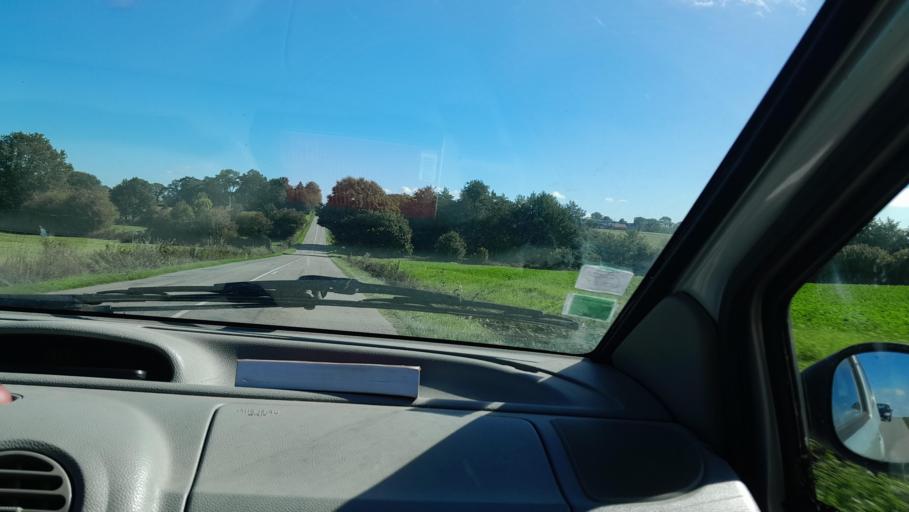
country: FR
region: Pays de la Loire
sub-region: Departement de la Mayenne
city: Cosse-le-Vivien
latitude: 47.9379
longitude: -0.8655
